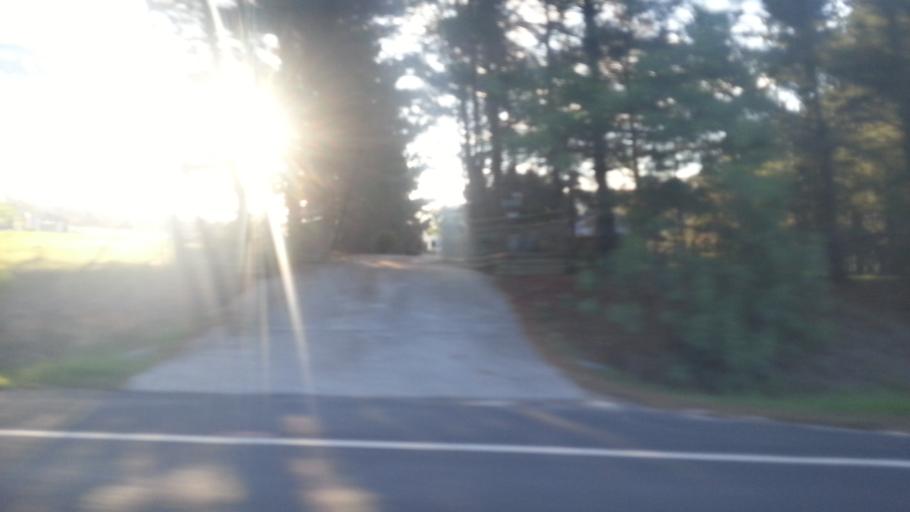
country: AU
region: New South Wales
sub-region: Wollondilly
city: Douglas Park
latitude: -34.1732
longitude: 150.7146
